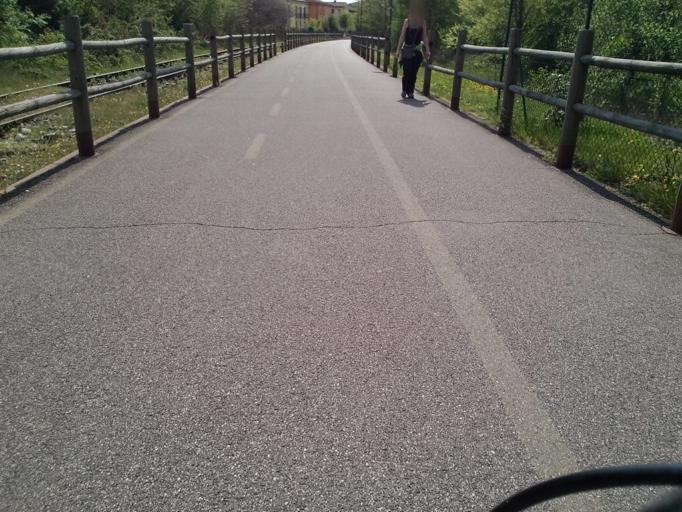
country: IT
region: Veneto
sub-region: Provincia di Verona
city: Verona
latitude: 45.4211
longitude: 10.9613
